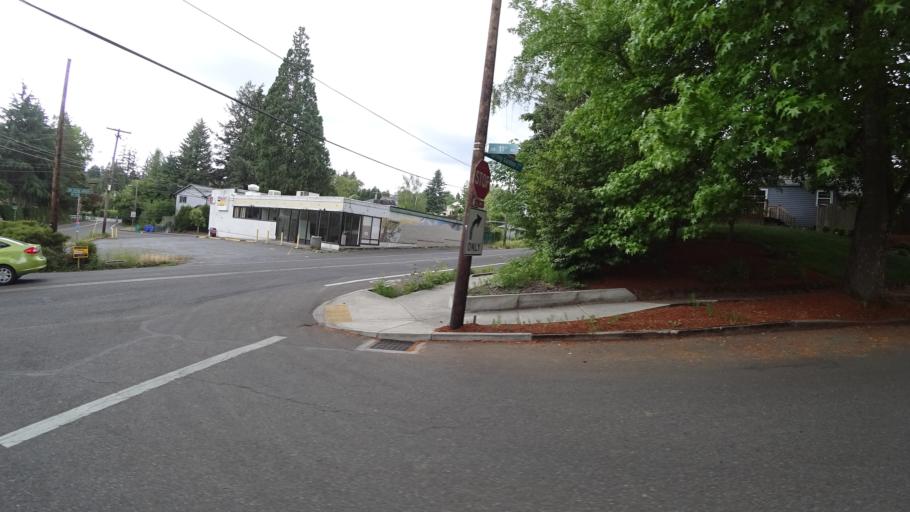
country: US
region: Oregon
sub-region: Clackamas County
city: Lake Oswego
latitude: 45.4632
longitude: -122.6899
